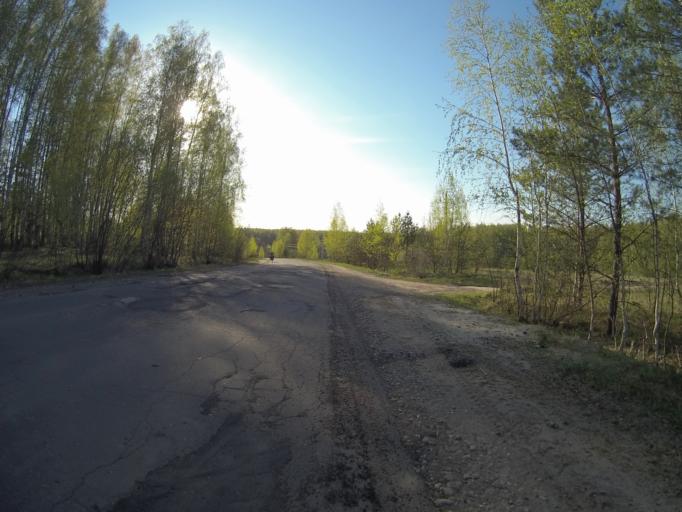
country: RU
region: Vladimir
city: Sudogda
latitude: 56.0739
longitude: 40.7852
